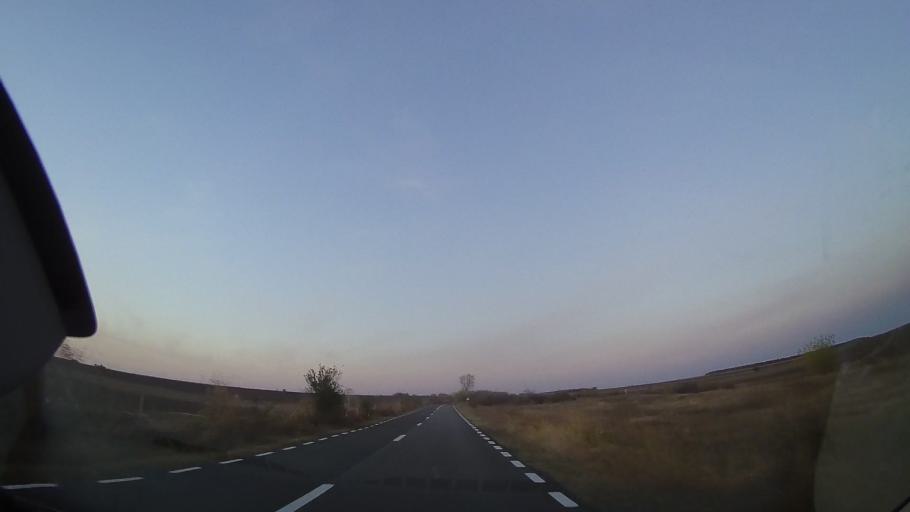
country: RO
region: Constanta
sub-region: Comuna Cobadin
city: Cobadin
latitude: 44.0296
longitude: 28.2619
